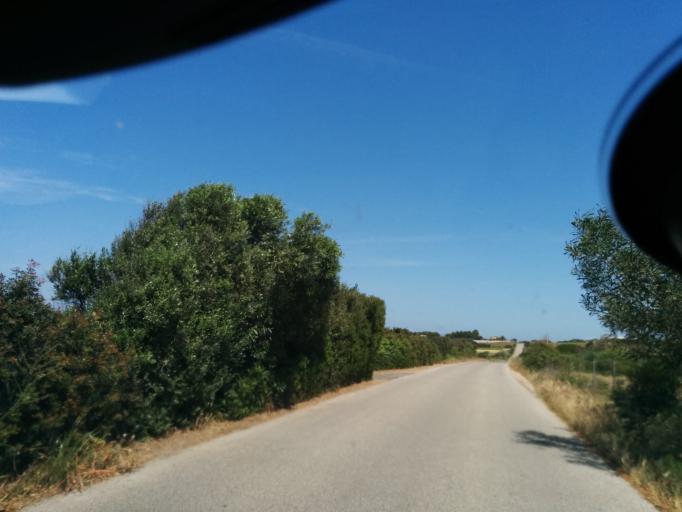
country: IT
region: Sardinia
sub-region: Provincia di Carbonia-Iglesias
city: Calasetta
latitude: 39.0806
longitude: 8.3662
